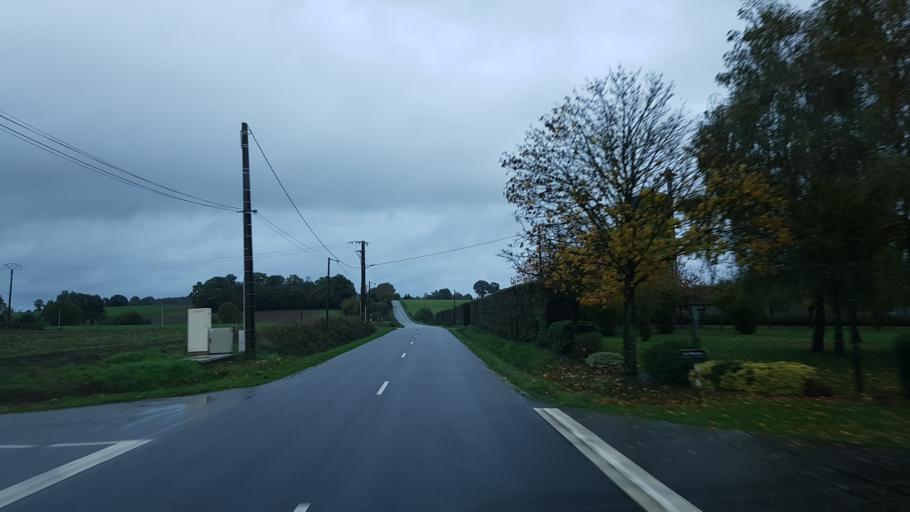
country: FR
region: Brittany
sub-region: Departement d'Ille-et-Vilaine
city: Balaze
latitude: 48.1472
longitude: -1.1581
